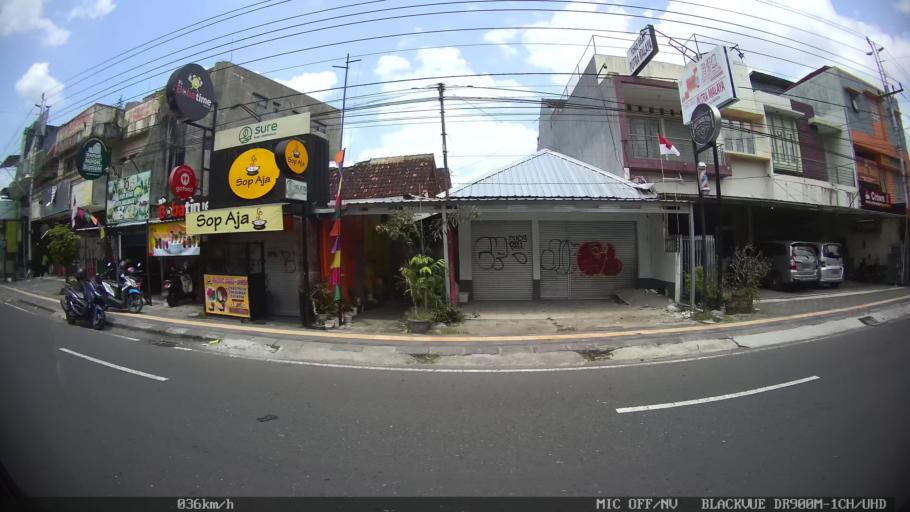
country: ID
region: Daerah Istimewa Yogyakarta
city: Yogyakarta
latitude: -7.7769
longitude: 110.3828
